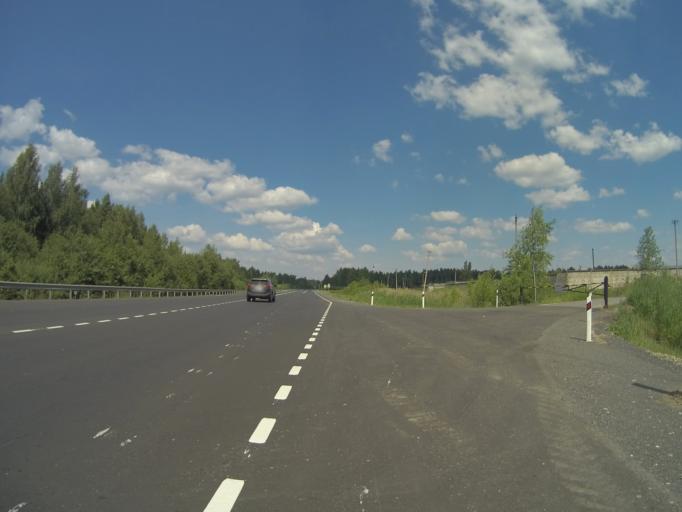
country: RU
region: Kostroma
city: Volgorechensk
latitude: 57.4141
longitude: 41.1968
